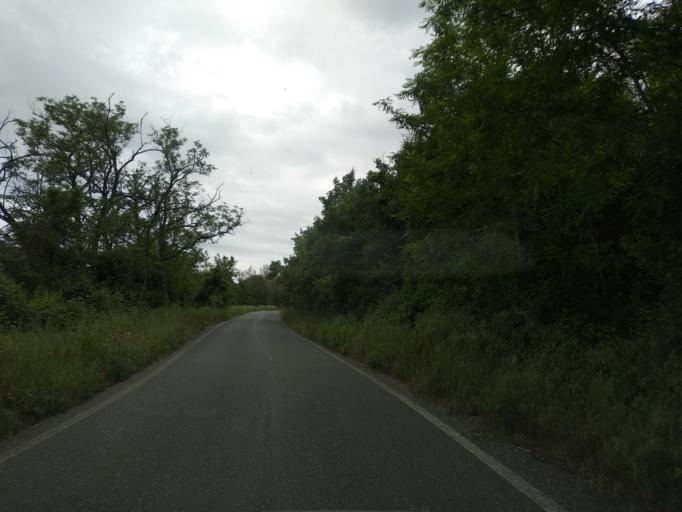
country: IT
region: Tuscany
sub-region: Provincia di Livorno
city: Collesalvetti
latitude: 43.5386
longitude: 10.4397
